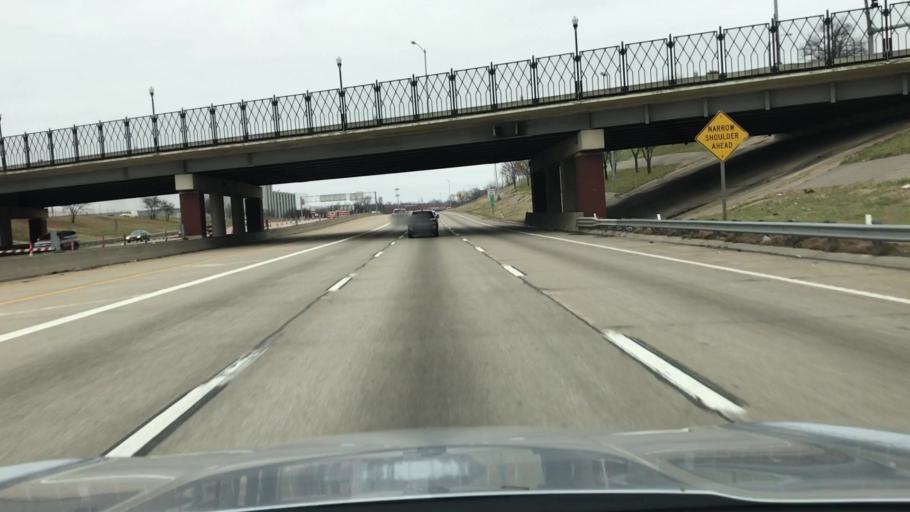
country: US
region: Missouri
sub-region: Saint Louis County
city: Pine Lawn
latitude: 38.6884
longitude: -90.2503
